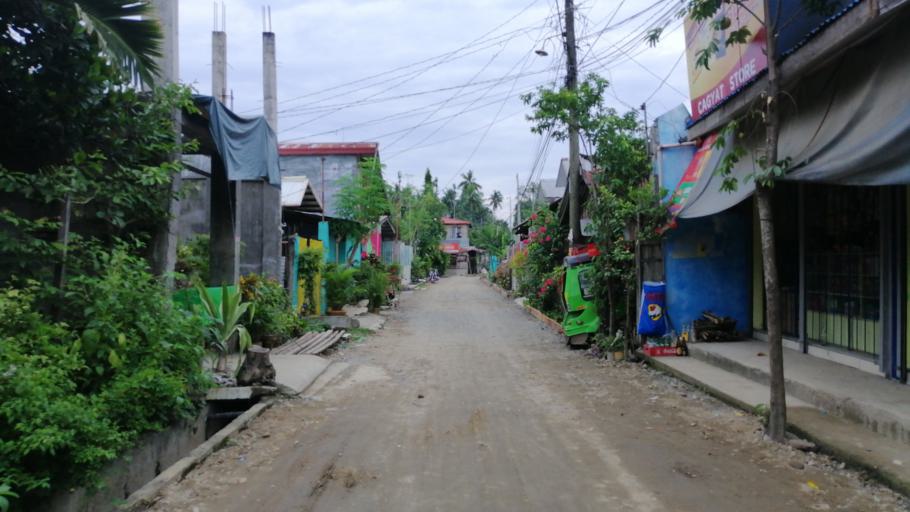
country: PH
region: Davao
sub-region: Province of Davao del Norte
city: Tagum
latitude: 7.4502
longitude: 125.8199
